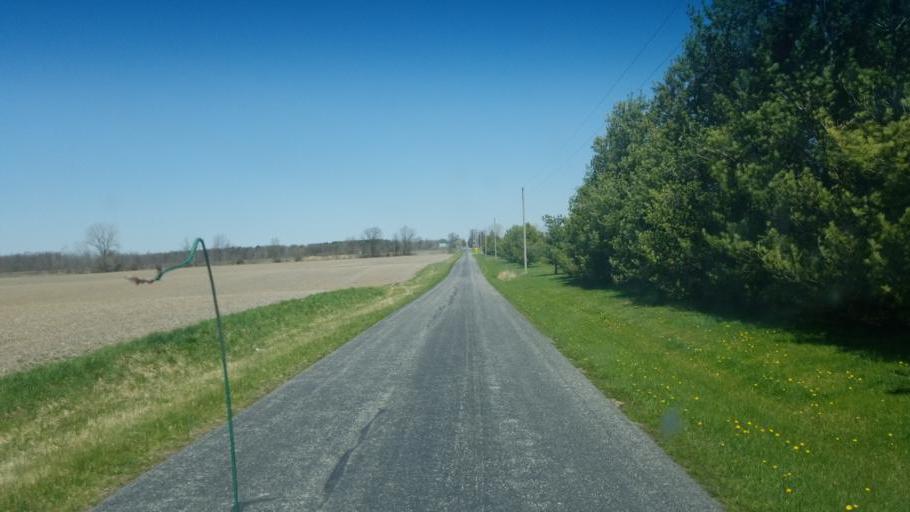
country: US
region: Ohio
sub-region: Huron County
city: New London
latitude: 41.0663
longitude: -82.4370
